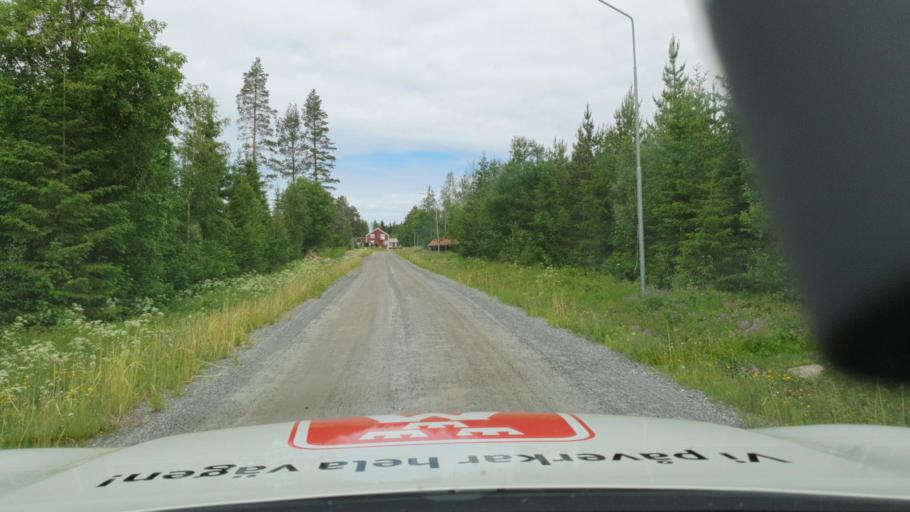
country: SE
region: Vaesterbotten
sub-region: Skelleftea Kommun
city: Langsele
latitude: 64.4758
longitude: 20.2614
